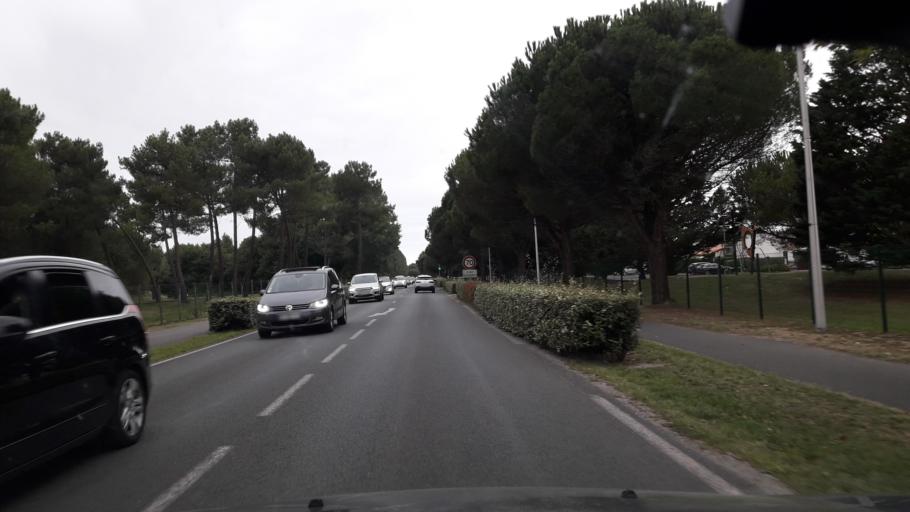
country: FR
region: Poitou-Charentes
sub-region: Departement de la Charente-Maritime
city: Les Mathes
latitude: 45.7012
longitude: -1.1699
